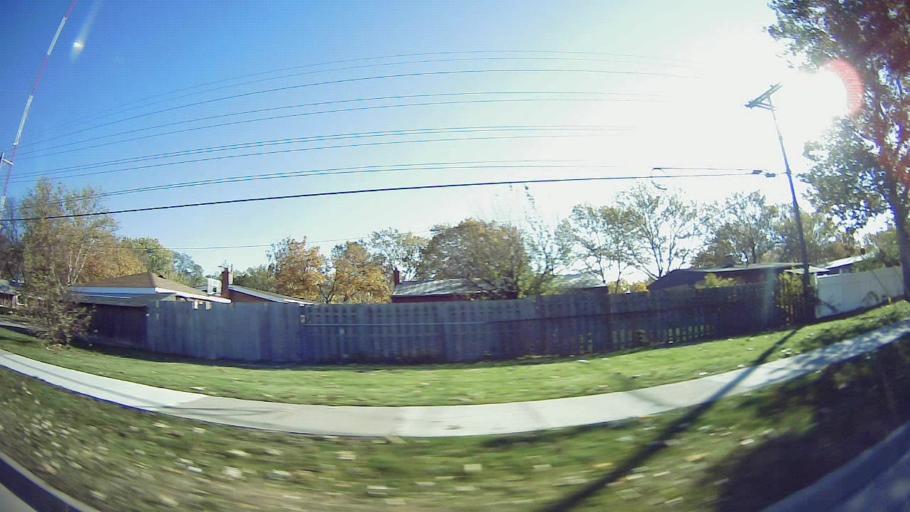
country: US
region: Michigan
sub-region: Oakland County
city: Oak Park
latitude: 42.4691
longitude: -83.2013
